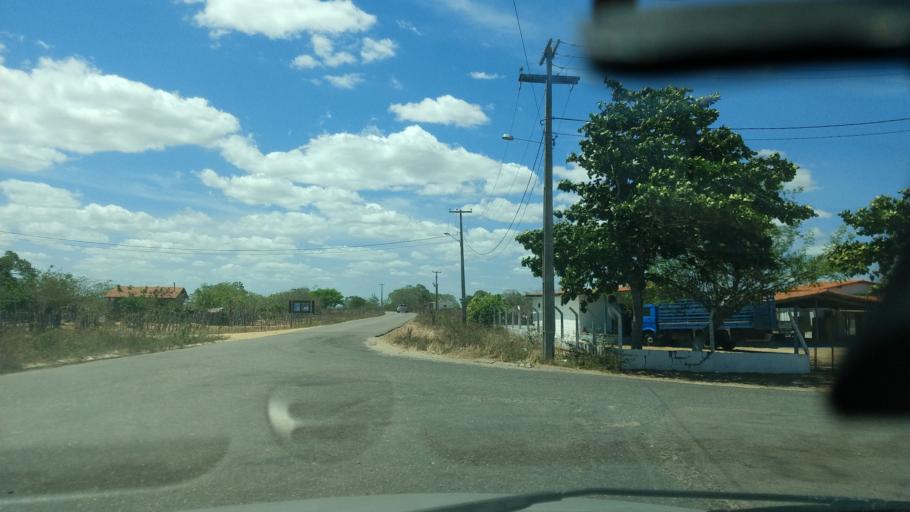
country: BR
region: Rio Grande do Norte
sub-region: Sao Paulo Do Potengi
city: Sao Paulo do Potengi
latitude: -5.9135
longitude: -35.7531
